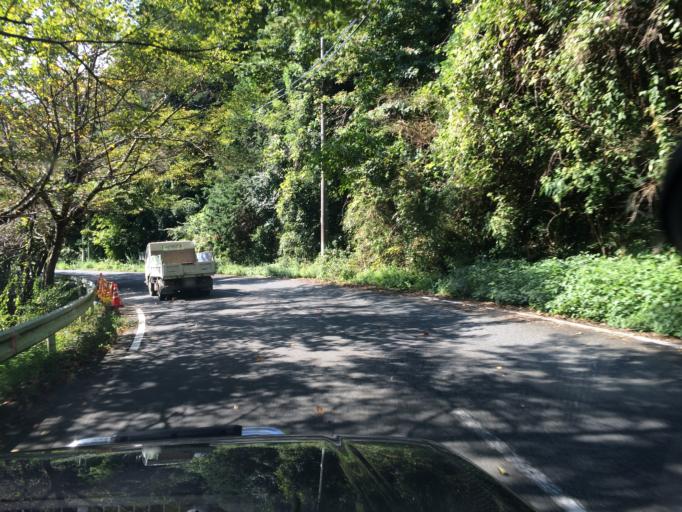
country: JP
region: Mie
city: Nabari
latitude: 34.7003
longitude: 135.9746
